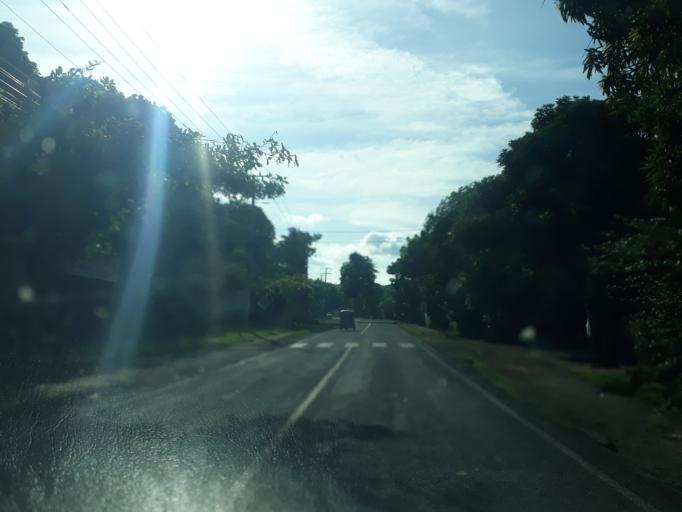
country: NI
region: Masaya
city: Masatepe
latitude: 11.9047
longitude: -86.1632
